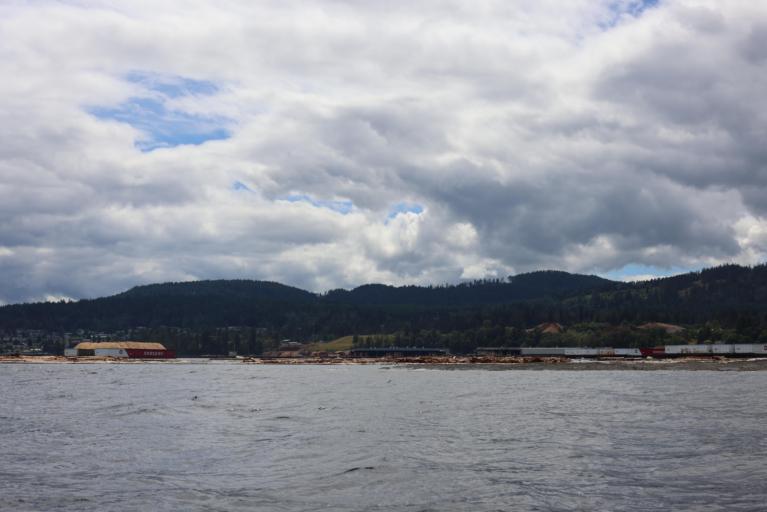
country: CA
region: British Columbia
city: North Cowichan
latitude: 48.8810
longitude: -123.6299
